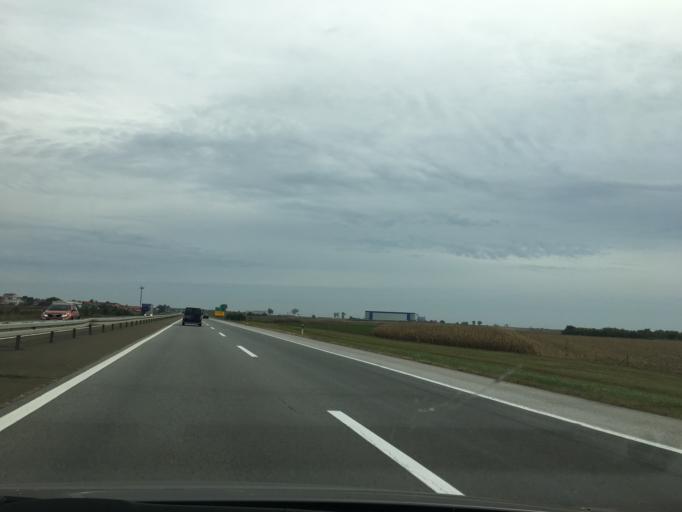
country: RS
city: Novi Banovci
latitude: 44.9498
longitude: 20.2701
